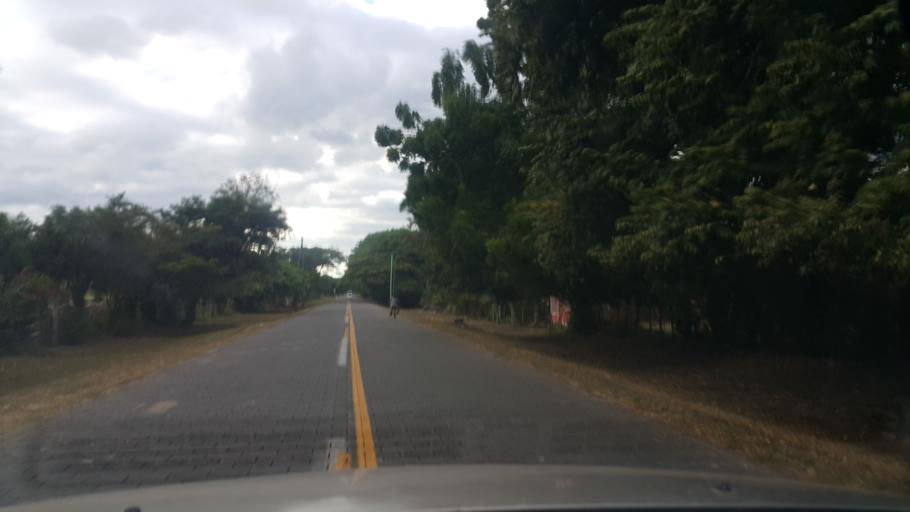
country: NI
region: Rivas
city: Moyogalpa
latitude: 11.4946
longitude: -85.6823
